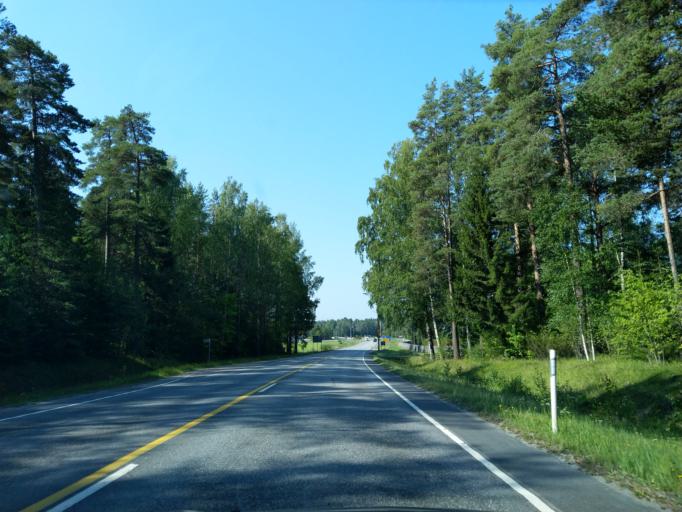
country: FI
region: Satakunta
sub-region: Pori
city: Noormarkku
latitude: 61.5984
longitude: 21.8710
